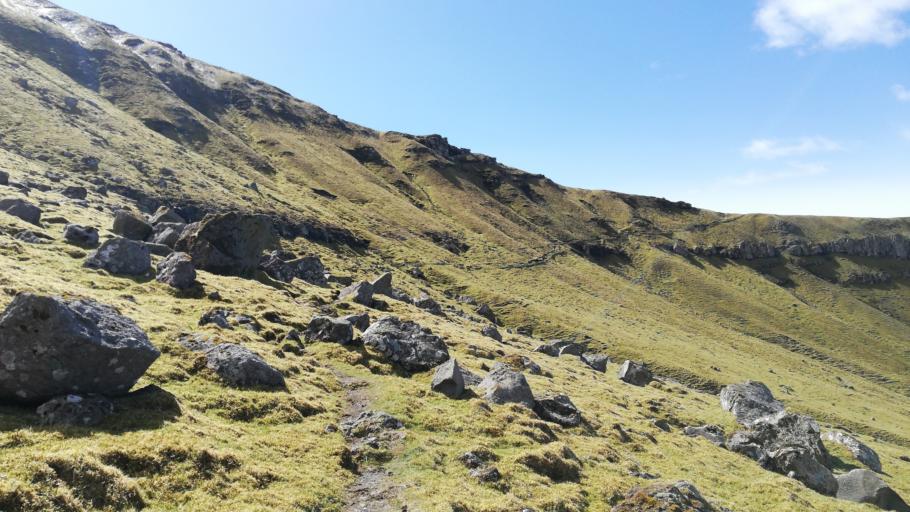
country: FO
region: Streymoy
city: Kollafjordhur
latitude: 62.0699
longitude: -6.9756
